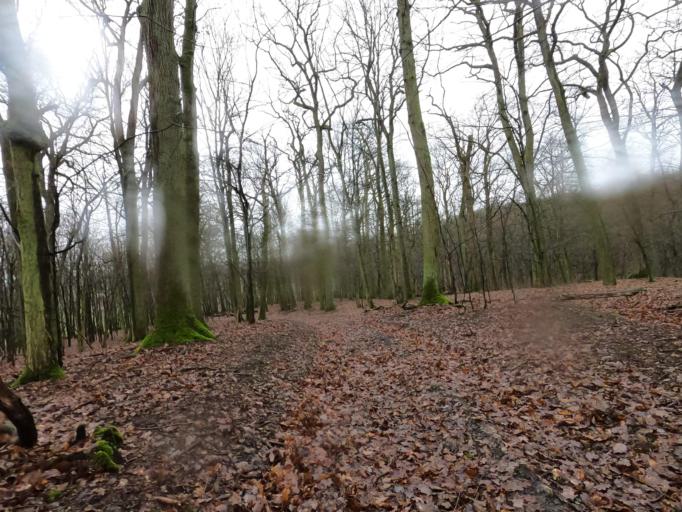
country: PL
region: Greater Poland Voivodeship
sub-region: Powiat pilski
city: Osiek nad Notecia
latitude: 53.1188
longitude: 17.2625
